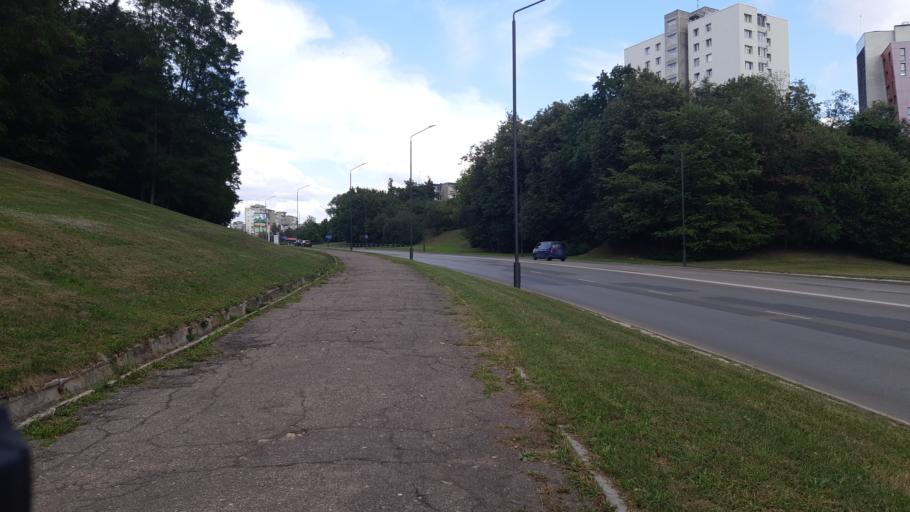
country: LT
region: Kauno apskritis
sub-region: Kaunas
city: Eiguliai
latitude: 54.9275
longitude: 23.9228
